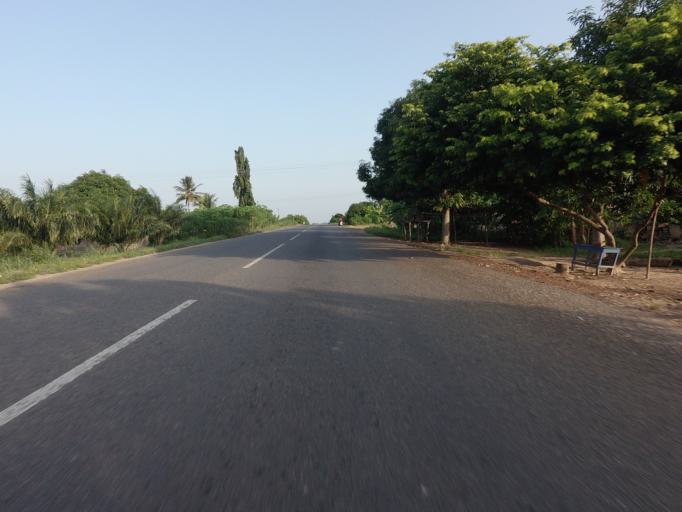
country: GH
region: Volta
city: Anloga
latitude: 6.0144
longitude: 0.6667
